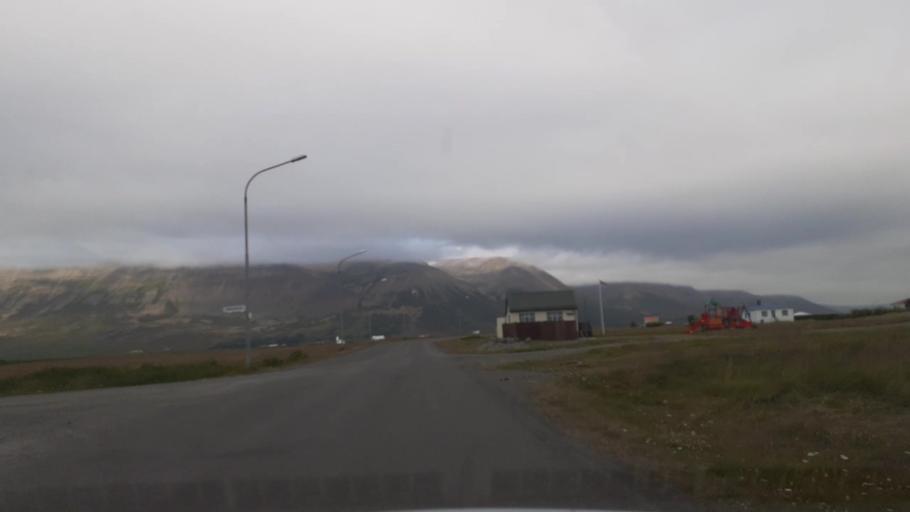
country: IS
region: Northwest
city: Saudarkrokur
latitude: 65.9005
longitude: -19.4222
